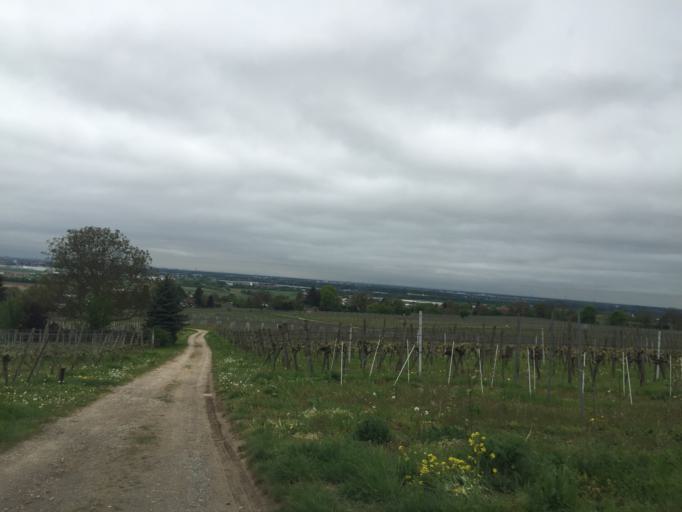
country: DE
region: Baden-Wuerttemberg
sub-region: Karlsruhe Region
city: Schriesheim
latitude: 49.5043
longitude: 8.6685
